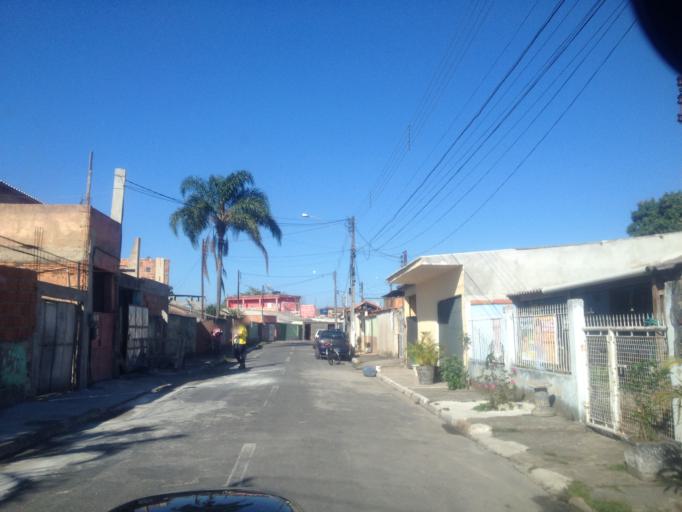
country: BR
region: Rio de Janeiro
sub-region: Porto Real
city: Porto Real
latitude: -22.4140
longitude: -44.3052
